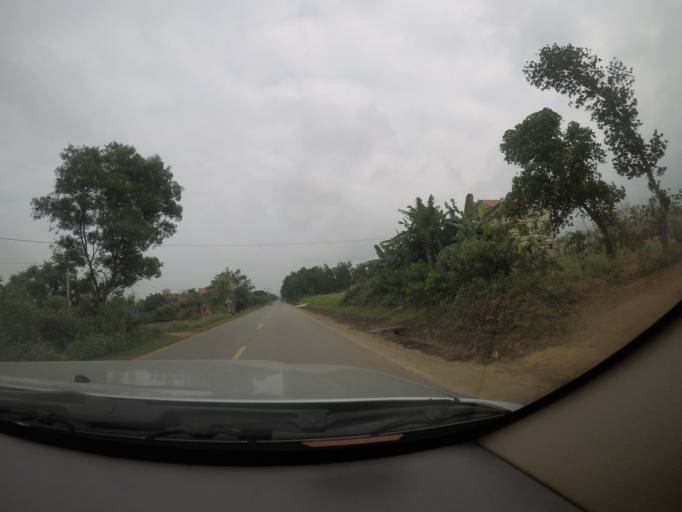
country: VN
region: Quang Binh
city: Hoan Lao
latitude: 17.5089
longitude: 106.4985
